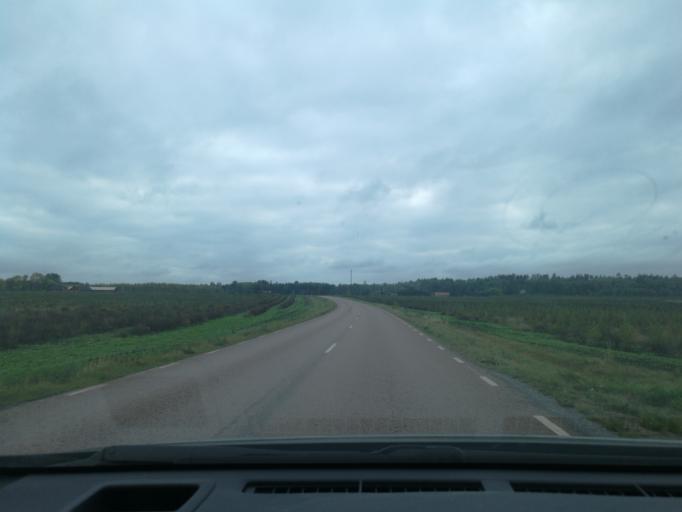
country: SE
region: Vaestmanland
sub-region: Vasteras
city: Tillberga
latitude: 59.7041
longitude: 16.6539
